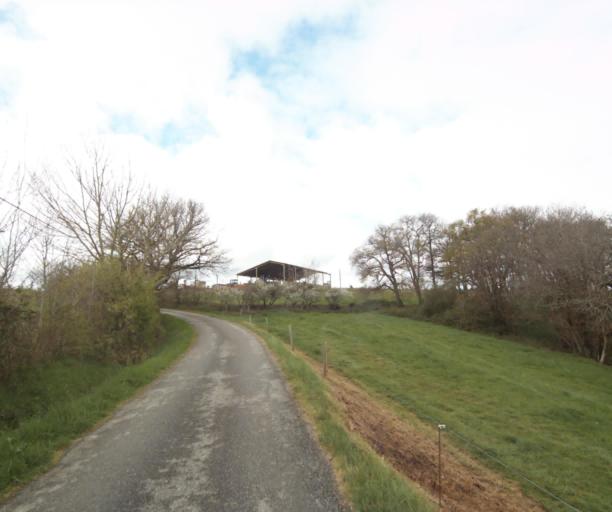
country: FR
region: Midi-Pyrenees
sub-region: Departement de l'Ariege
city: Saverdun
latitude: 43.2181
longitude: 1.5399
